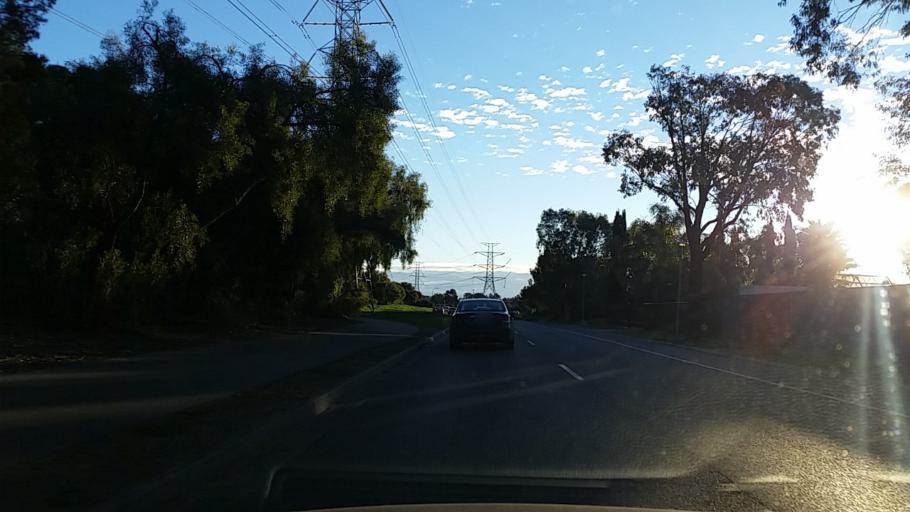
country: AU
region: South Australia
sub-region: Salisbury
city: Salisbury
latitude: -34.7599
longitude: 138.6255
